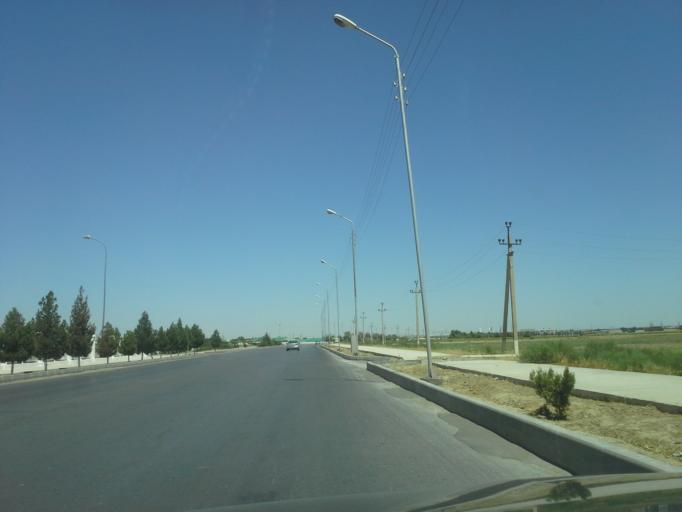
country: TM
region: Ahal
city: Abadan
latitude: 38.0347
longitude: 58.2701
